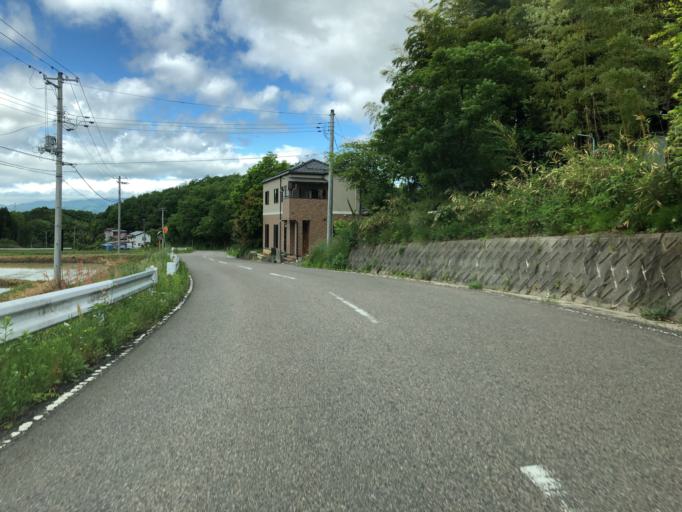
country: JP
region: Fukushima
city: Miharu
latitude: 37.4691
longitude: 140.4659
